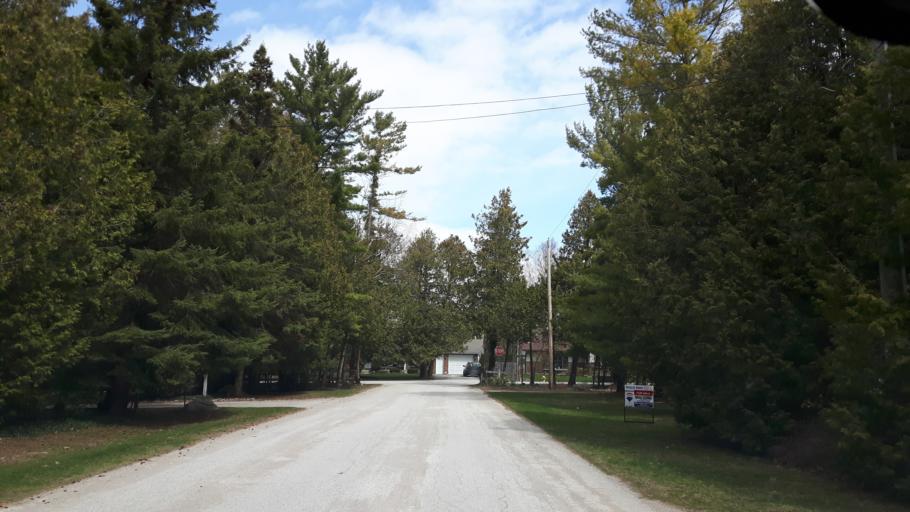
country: CA
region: Ontario
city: Bluewater
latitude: 43.5562
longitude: -81.6973
